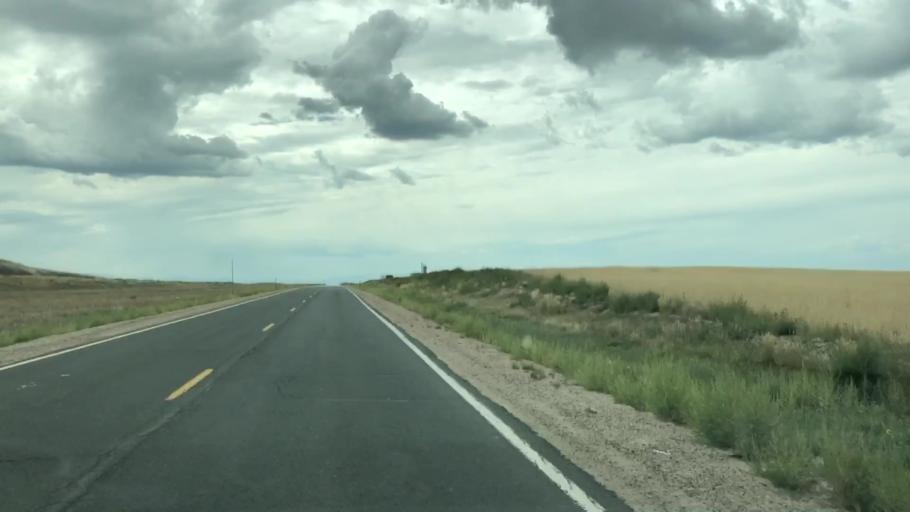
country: US
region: Colorado
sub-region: Adams County
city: Aurora
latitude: 39.7984
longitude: -104.6978
